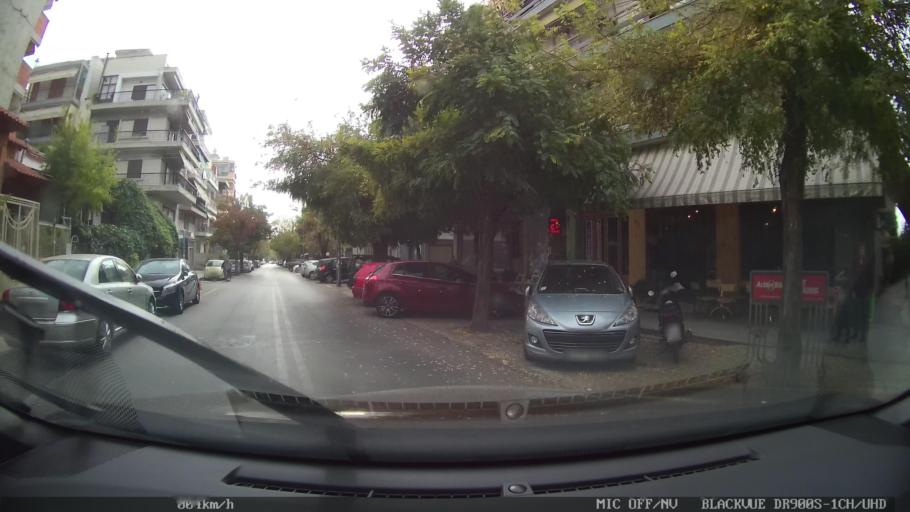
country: GR
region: Central Macedonia
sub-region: Nomos Thessalonikis
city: Triandria
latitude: 40.6099
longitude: 22.9747
